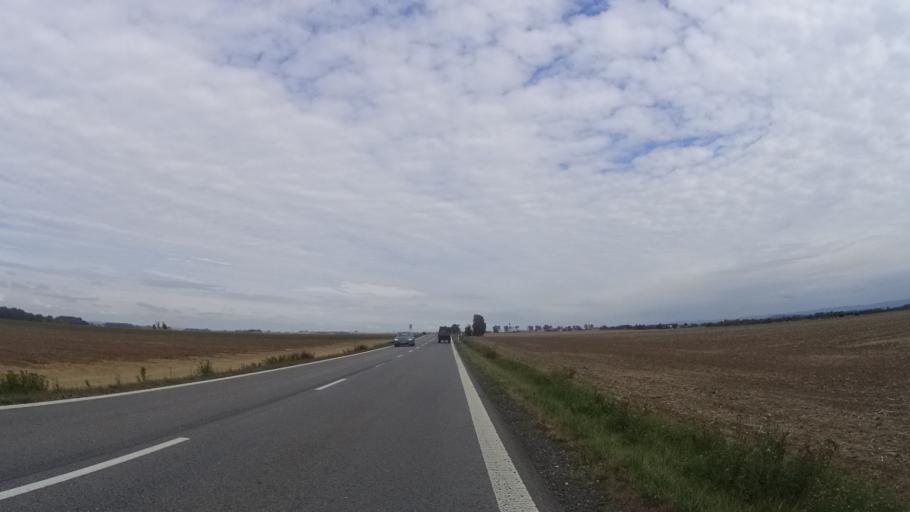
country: CZ
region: Olomoucky
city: Tovacov
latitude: 49.4427
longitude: 17.2804
